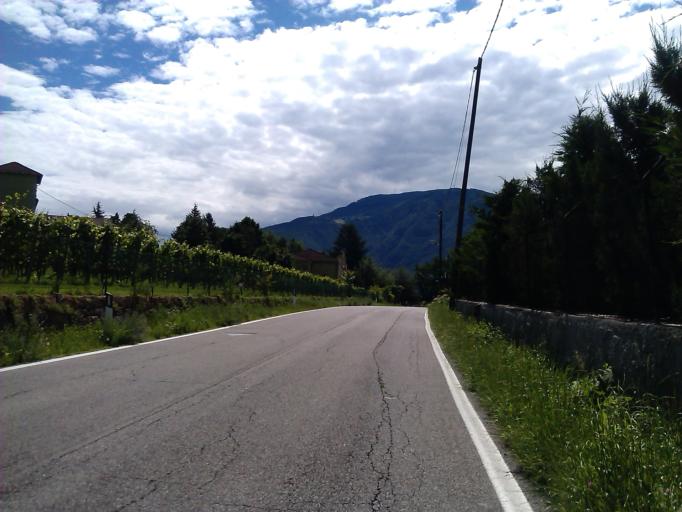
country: IT
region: Trentino-Alto Adige
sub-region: Bolzano
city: Bolzano
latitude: 46.5023
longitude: 11.3028
